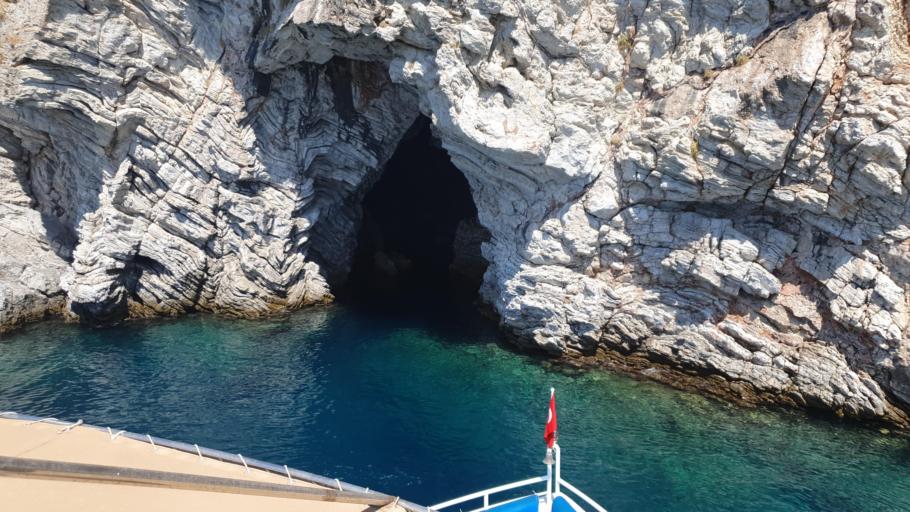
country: TR
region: Mugla
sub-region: Marmaris
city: Marmaris
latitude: 36.7920
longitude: 28.2844
